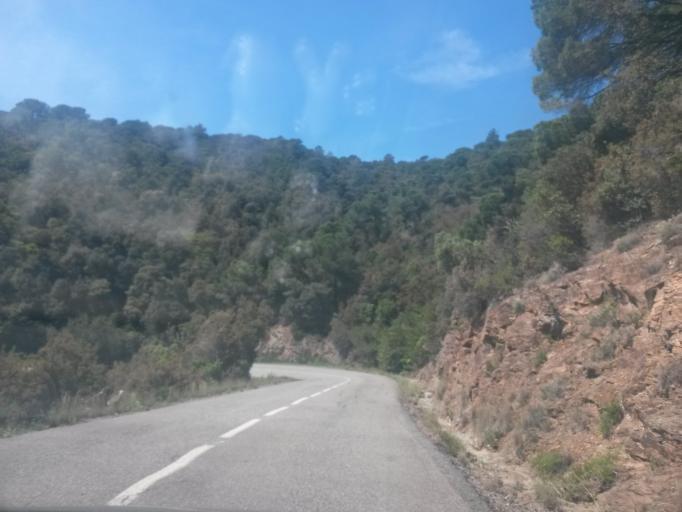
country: ES
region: Catalonia
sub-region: Provincia de Girona
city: Sant Marti Vell
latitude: 41.9827
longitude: 2.9323
